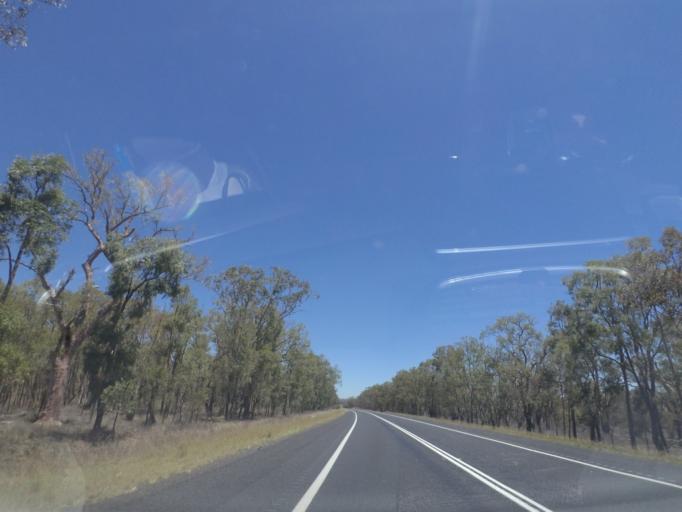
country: AU
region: New South Wales
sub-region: Warrumbungle Shire
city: Coonabarabran
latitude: -31.2095
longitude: 149.3310
